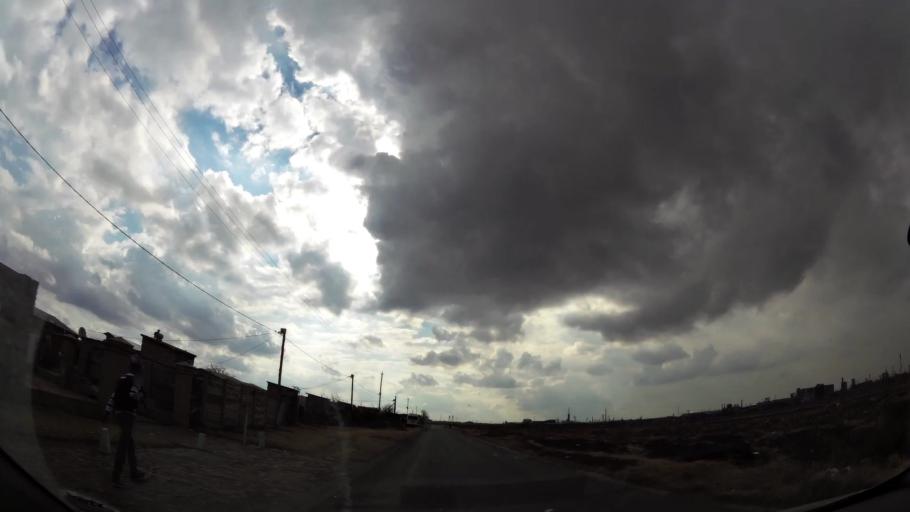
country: ZA
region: Orange Free State
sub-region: Fezile Dabi District Municipality
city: Sasolburg
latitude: -26.8420
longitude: 27.8655
